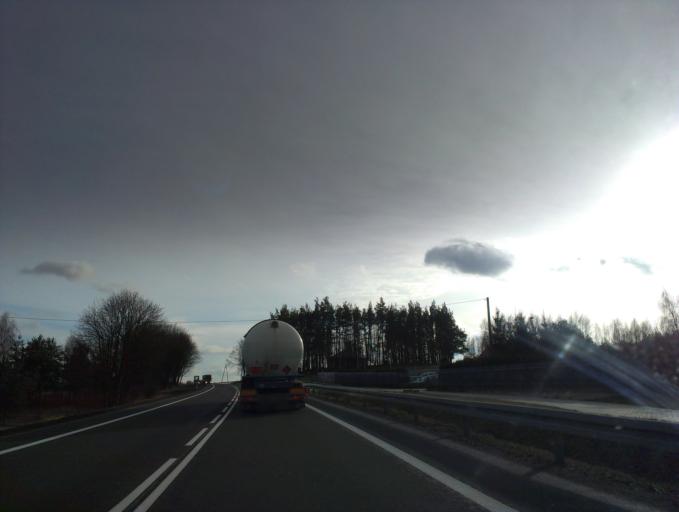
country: PL
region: Kujawsko-Pomorskie
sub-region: Powiat lipnowski
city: Kikol
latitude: 52.8943
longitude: 19.1235
